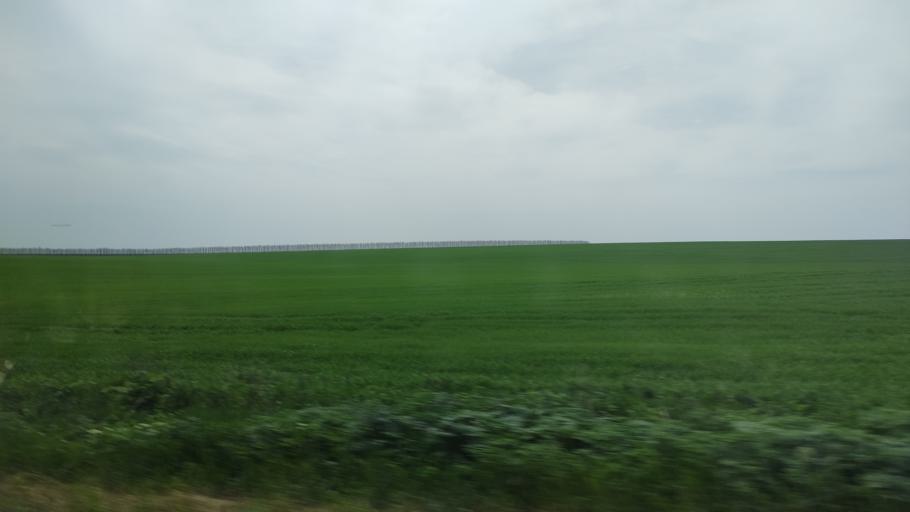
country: RO
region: Constanta
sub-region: Comuna Deleni
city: Pietreni
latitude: 44.0852
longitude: 28.1047
